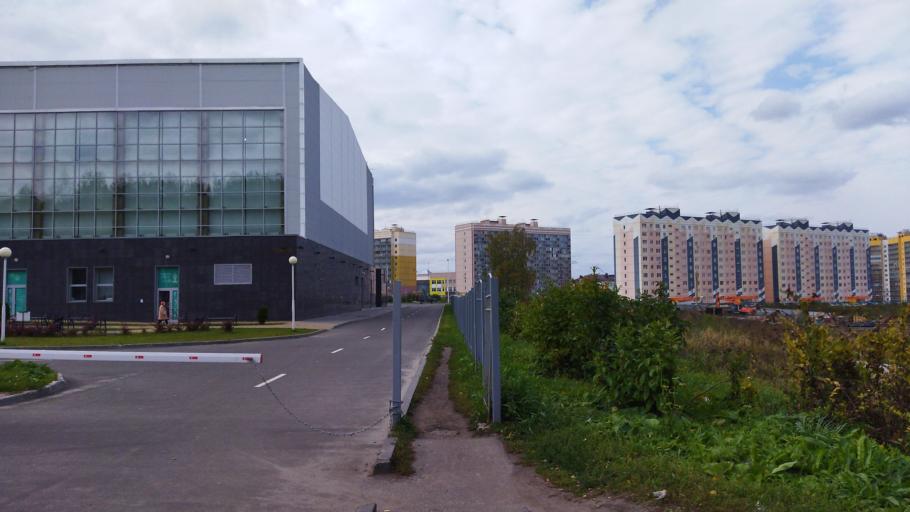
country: RU
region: Tomsk
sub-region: Tomskiy Rayon
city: Tomsk
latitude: 56.4944
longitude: 85.0603
